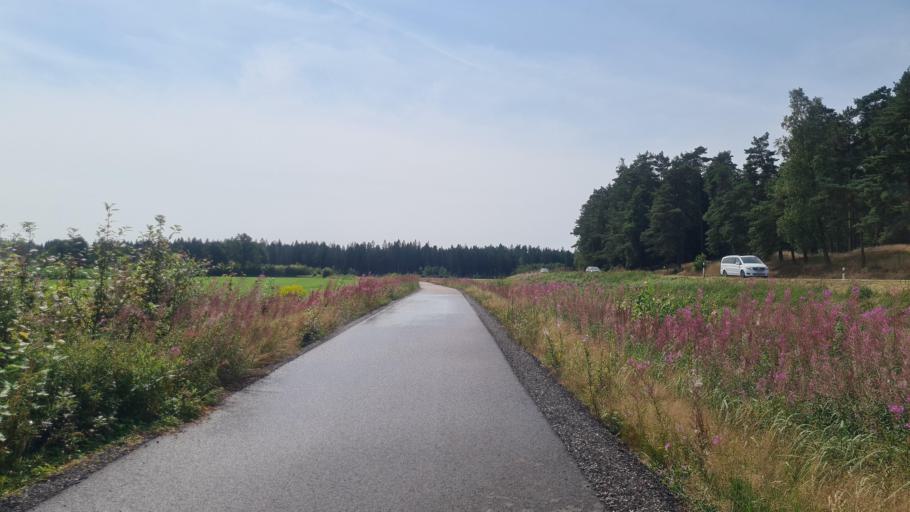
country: SE
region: Kronoberg
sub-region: Ljungby Kommun
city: Lagan
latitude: 56.8689
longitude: 13.9781
